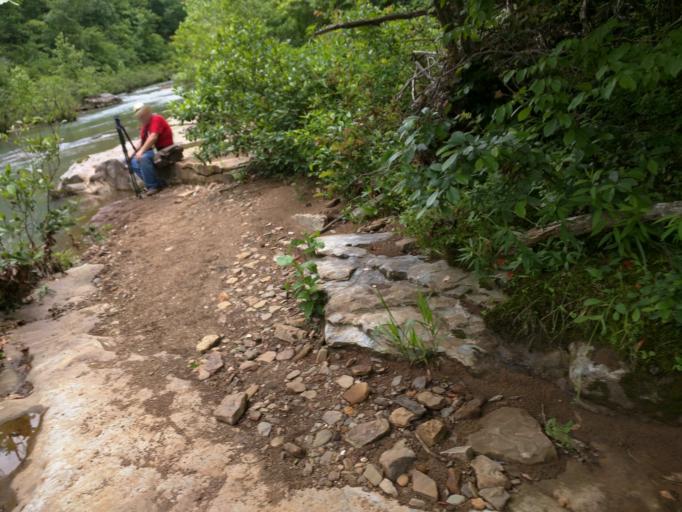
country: US
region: Arkansas
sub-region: Madison County
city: Huntsville
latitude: 35.9010
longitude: -93.5746
